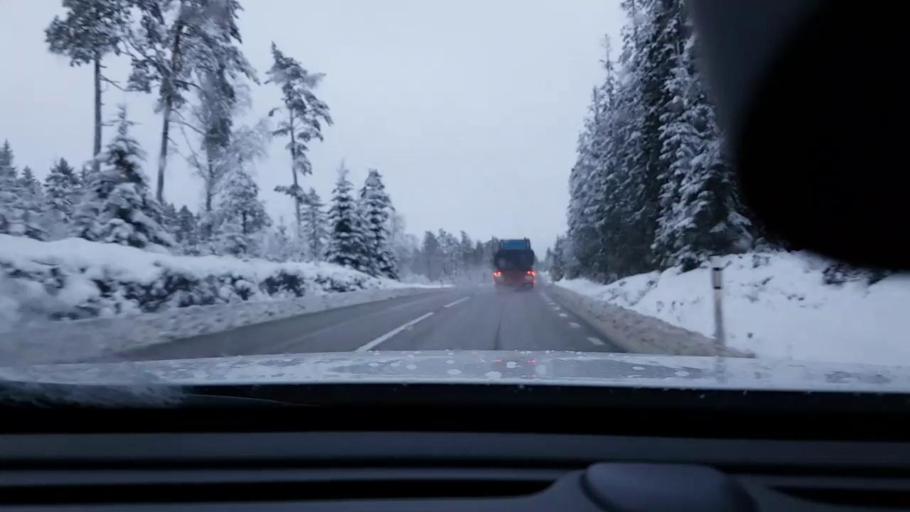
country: SE
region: Vaestra Goetaland
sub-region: Vargarda Kommun
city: Jonstorp
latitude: 57.8394
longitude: 12.6864
